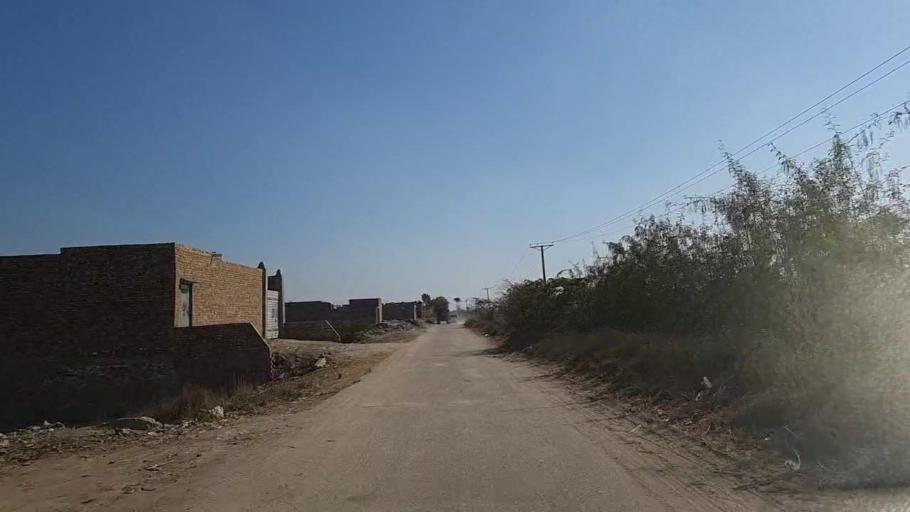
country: PK
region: Sindh
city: Nawabshah
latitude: 26.2415
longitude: 68.4235
